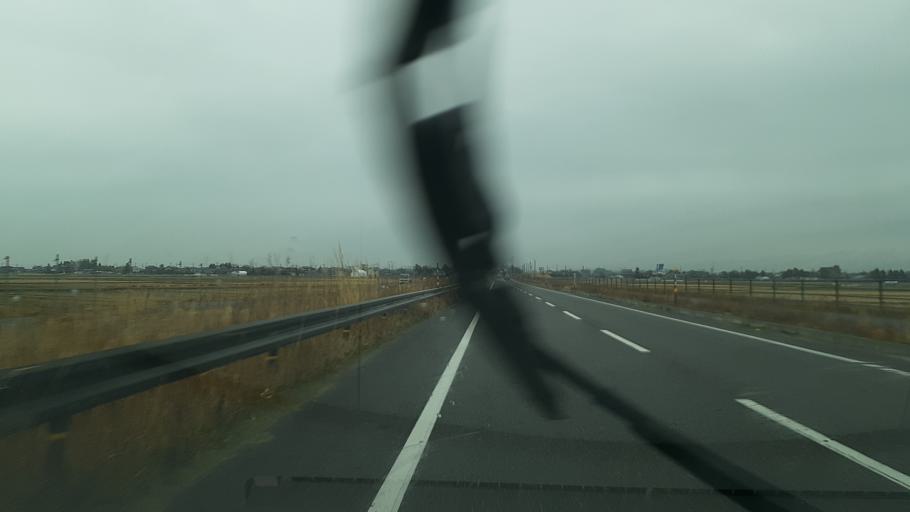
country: JP
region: Niigata
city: Kameda-honcho
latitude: 37.8724
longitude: 139.1519
